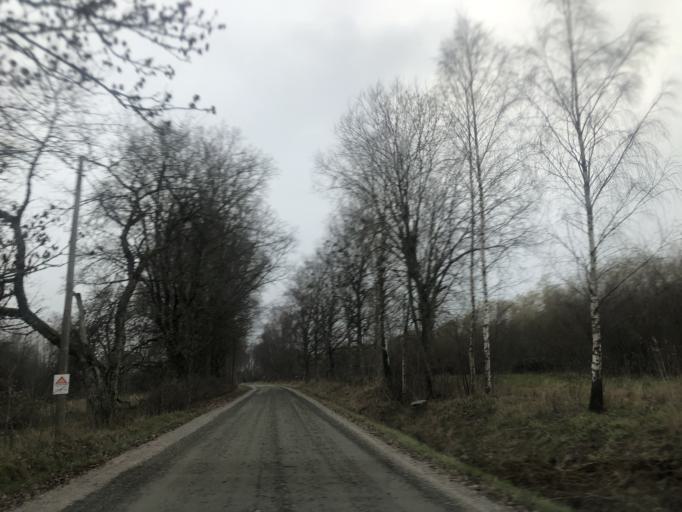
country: SE
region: Vaestra Goetaland
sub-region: Tranemo Kommun
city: Limmared
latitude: 57.6572
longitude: 13.3589
